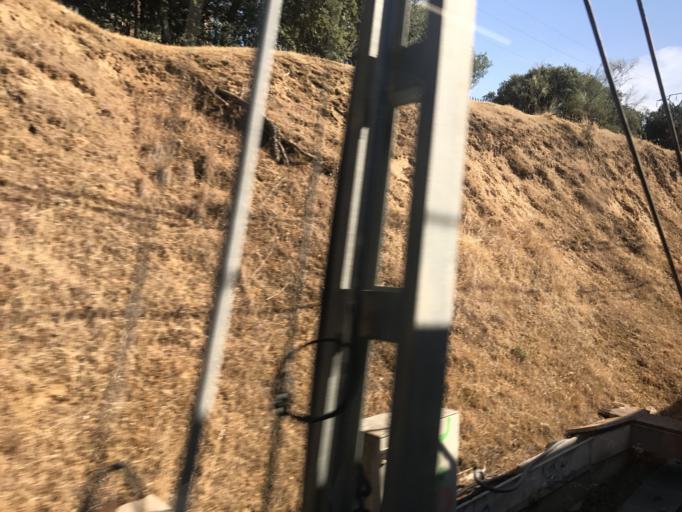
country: ES
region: Madrid
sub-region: Provincia de Madrid
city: Latina
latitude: 40.4054
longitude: -3.7578
